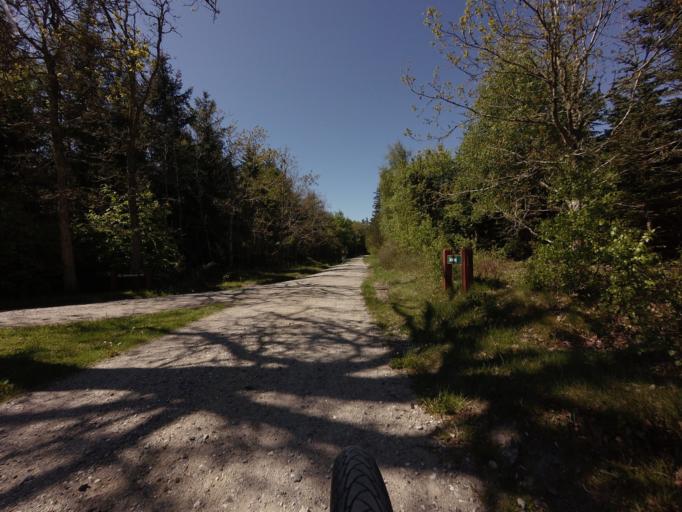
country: DK
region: North Denmark
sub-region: Jammerbugt Kommune
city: Pandrup
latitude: 57.2429
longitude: 9.5972
